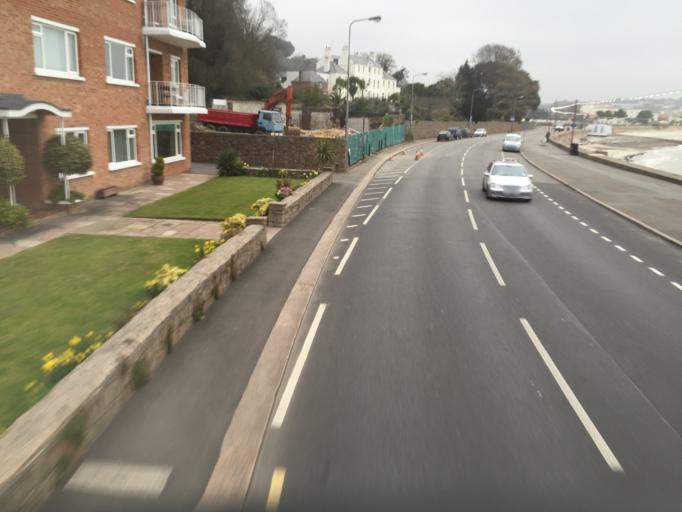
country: JE
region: St Helier
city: Saint Helier
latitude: 49.1906
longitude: -2.1685
